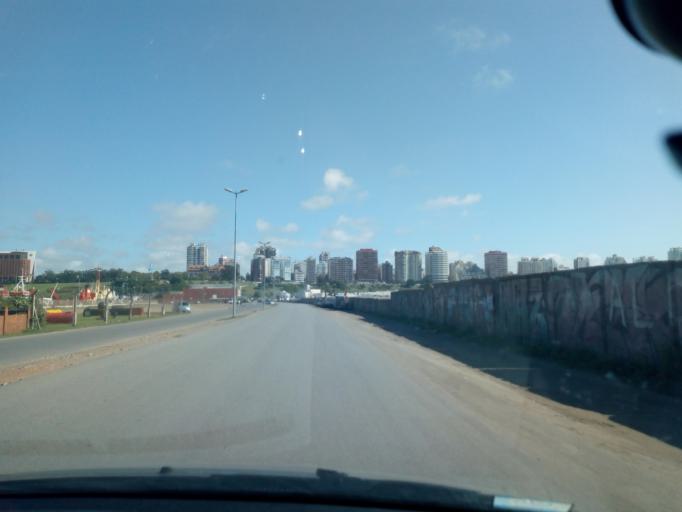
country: AR
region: Buenos Aires
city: Mar del Plata
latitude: -38.0337
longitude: -57.5282
